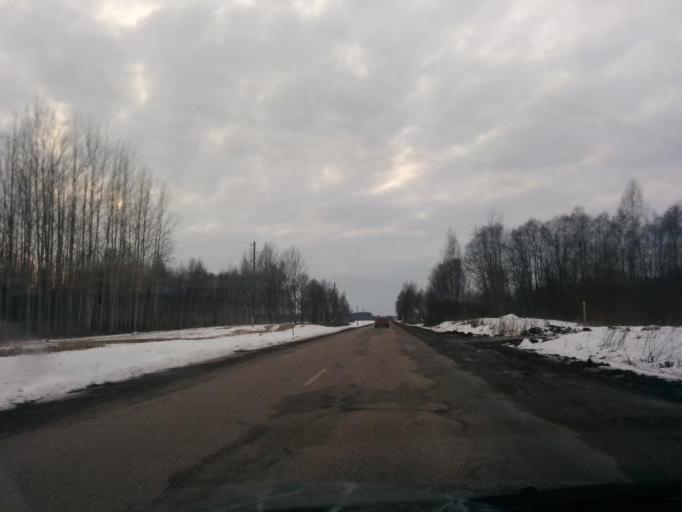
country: LV
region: Gulbenes Rajons
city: Gulbene
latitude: 57.1895
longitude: 26.8858
